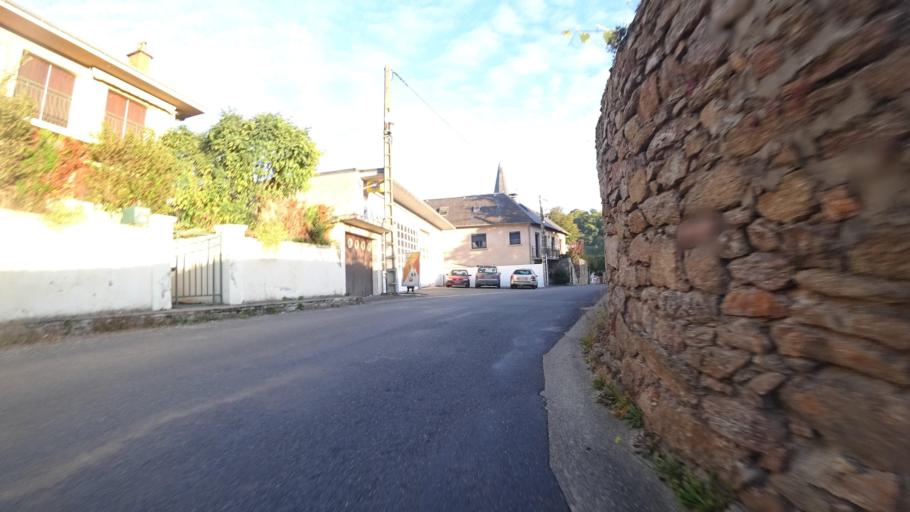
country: FR
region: Midi-Pyrenees
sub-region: Departement de l'Aveyron
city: Le Monastere
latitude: 44.3433
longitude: 2.5770
